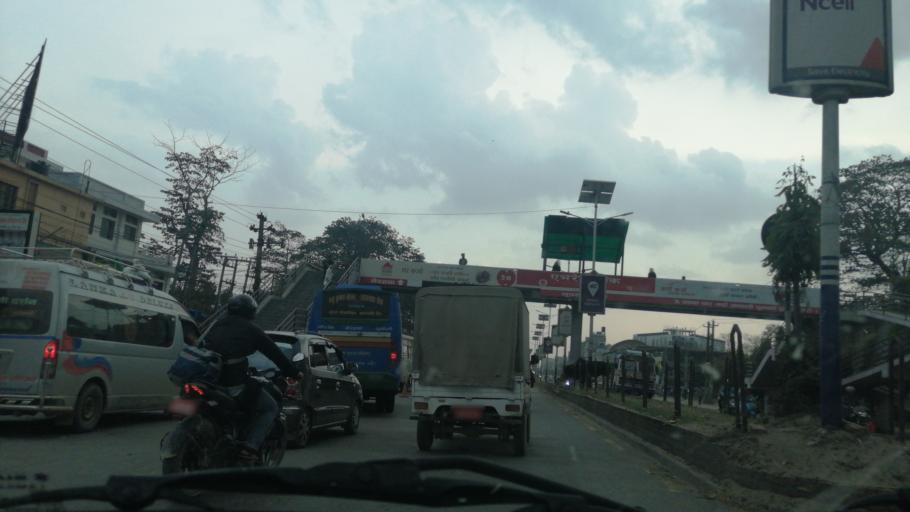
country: NP
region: Western Region
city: Butwal
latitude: 27.6962
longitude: 83.4651
